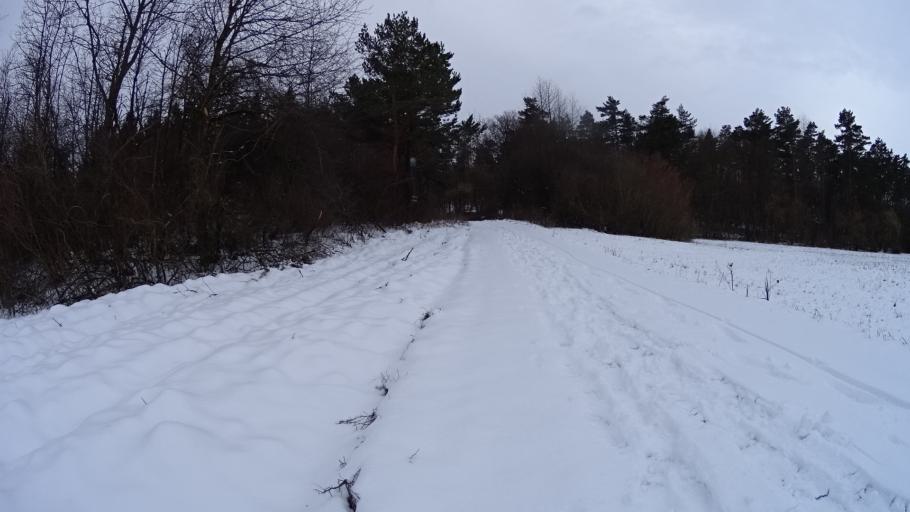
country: AT
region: Lower Austria
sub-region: Politischer Bezirk Korneuburg
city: Niederhollabrunn
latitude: 48.4254
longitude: 16.2864
